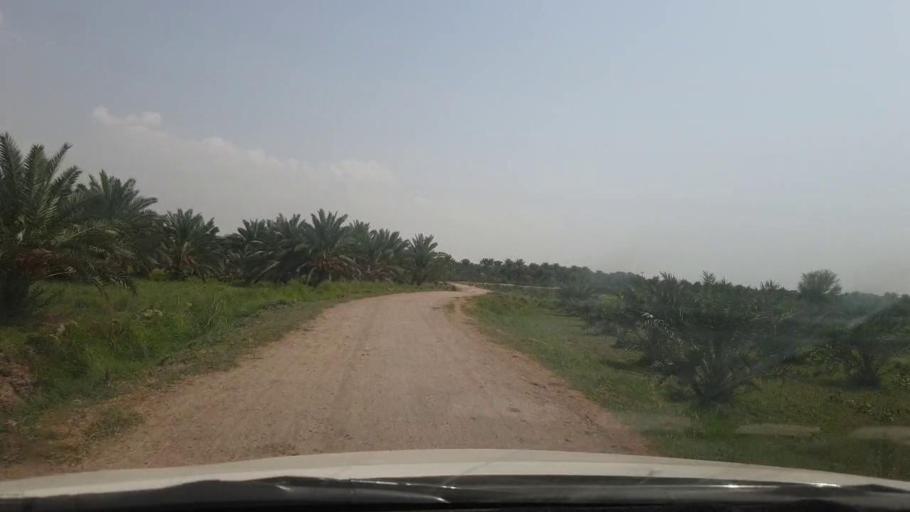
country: PK
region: Sindh
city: Khairpur
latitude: 27.5558
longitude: 68.8389
